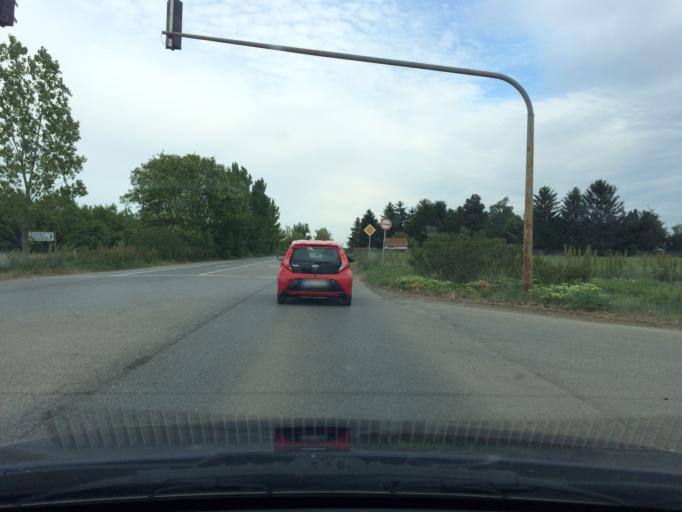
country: HU
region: Szabolcs-Szatmar-Bereg
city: Tiszavasvari
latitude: 47.9315
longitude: 21.3853
